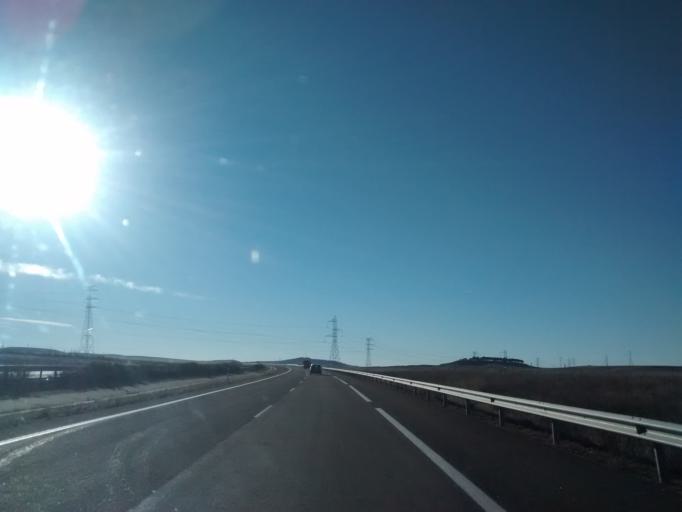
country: ES
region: Castille and Leon
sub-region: Provincia de Palencia
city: Herrera de Pisuerga
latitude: 42.5882
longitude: -4.3496
